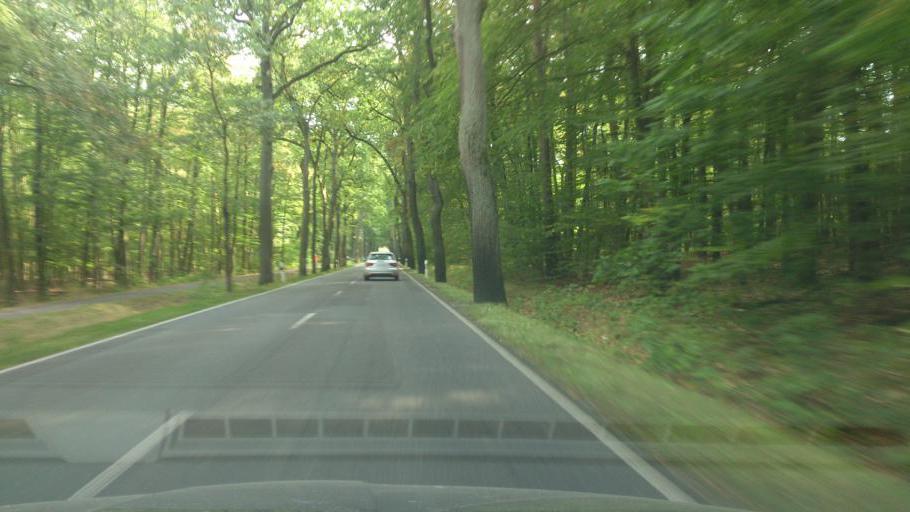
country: DE
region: Berlin
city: Wannsee
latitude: 52.3484
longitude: 13.1510
